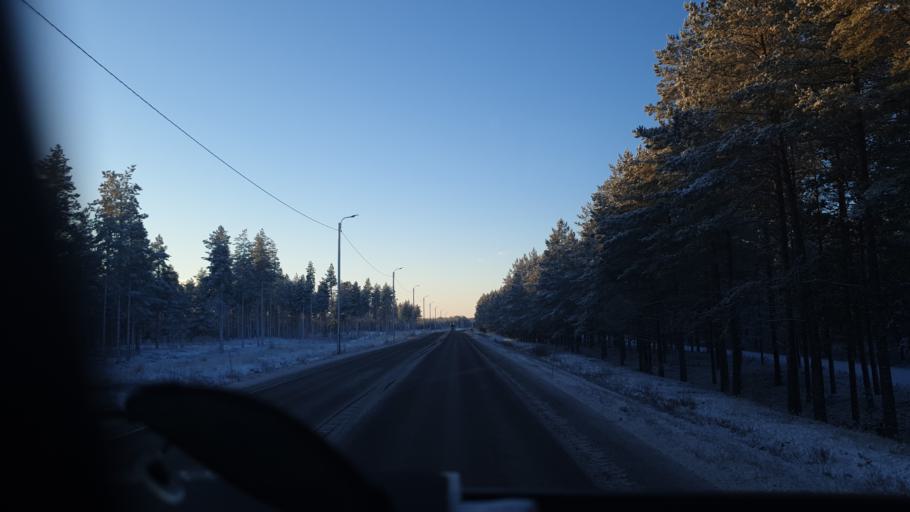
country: FI
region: Northern Ostrobothnia
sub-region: Ylivieska
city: Kalajoki
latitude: 64.2349
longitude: 23.8283
